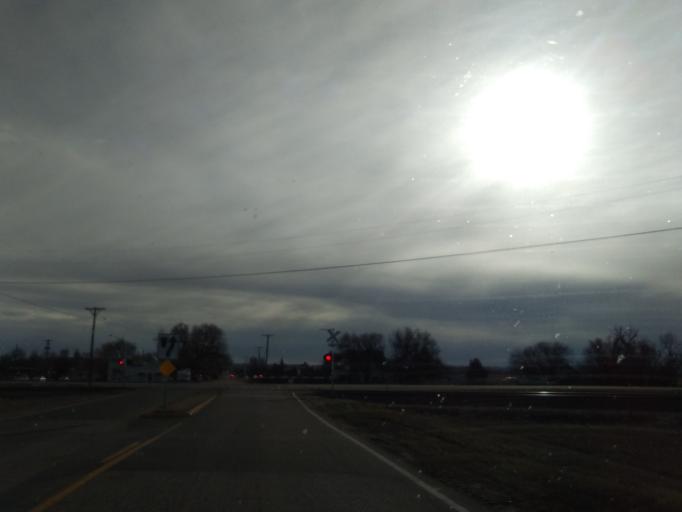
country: US
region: Nebraska
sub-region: Scotts Bluff County
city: Gering
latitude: 41.7854
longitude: -103.5191
